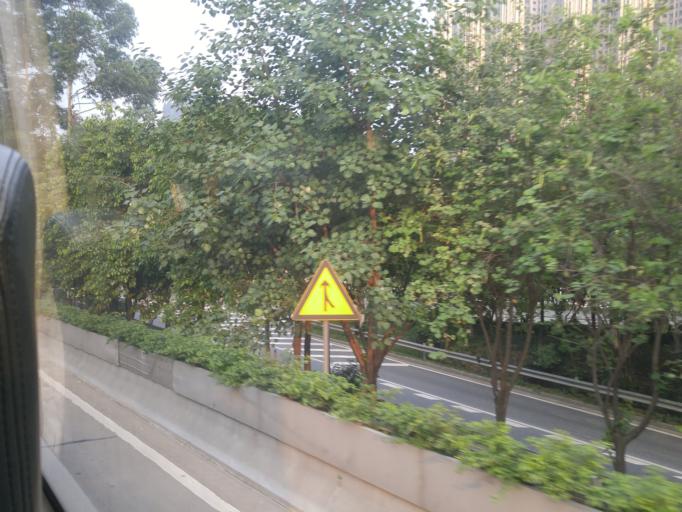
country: CN
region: Guangdong
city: Foshan
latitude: 23.0700
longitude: 113.1362
